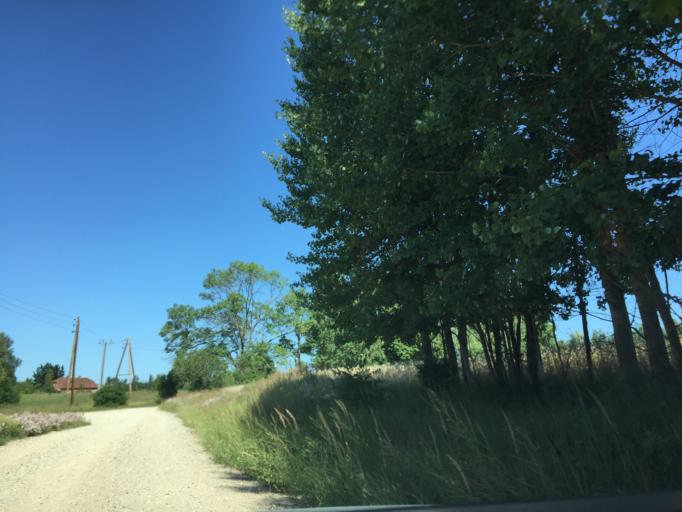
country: LV
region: Talsu Rajons
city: Stende
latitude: 57.1558
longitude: 22.2934
